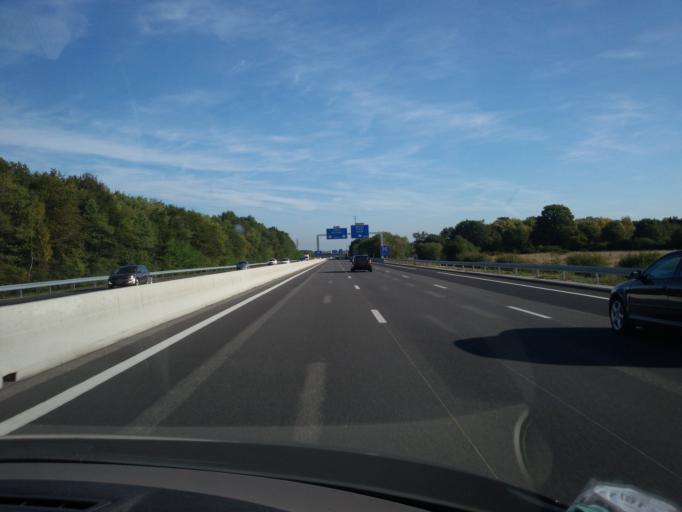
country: FR
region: Centre
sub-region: Departement du Loir-et-Cher
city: Theillay
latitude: 47.2773
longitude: 2.0429
